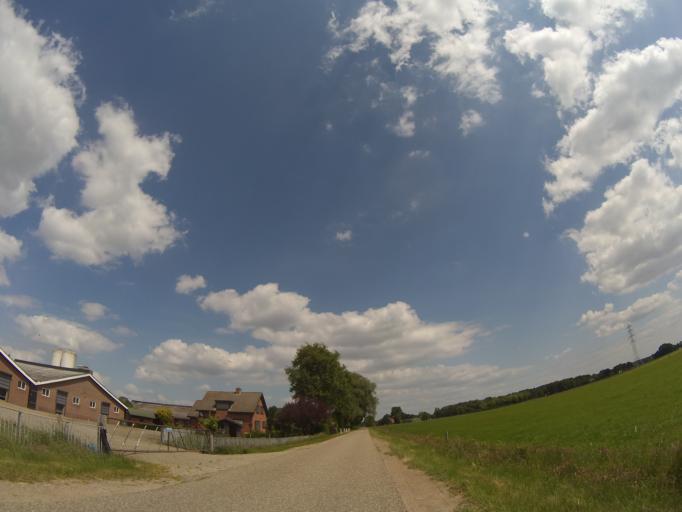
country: NL
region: Gelderland
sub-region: Gemeente Barneveld
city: Voorthuizen
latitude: 52.1998
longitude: 5.6297
